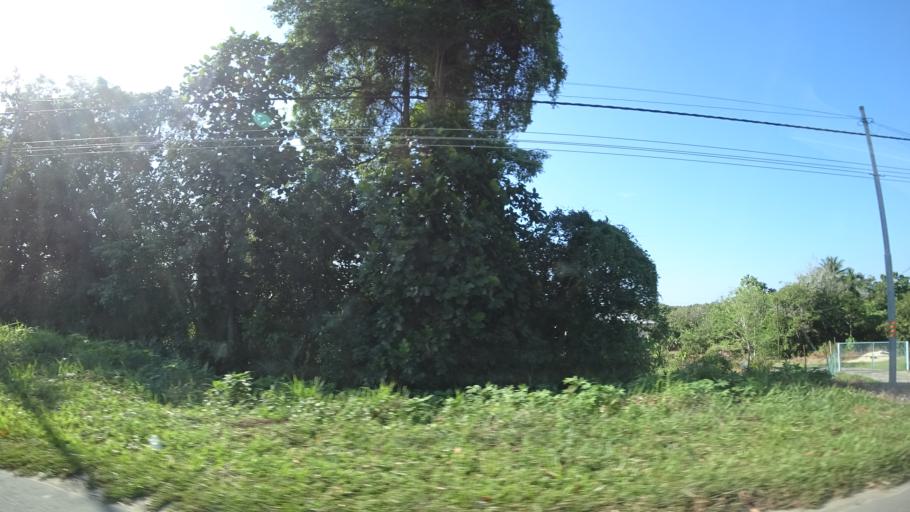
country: BN
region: Tutong
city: Tutong
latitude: 4.6908
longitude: 114.5123
